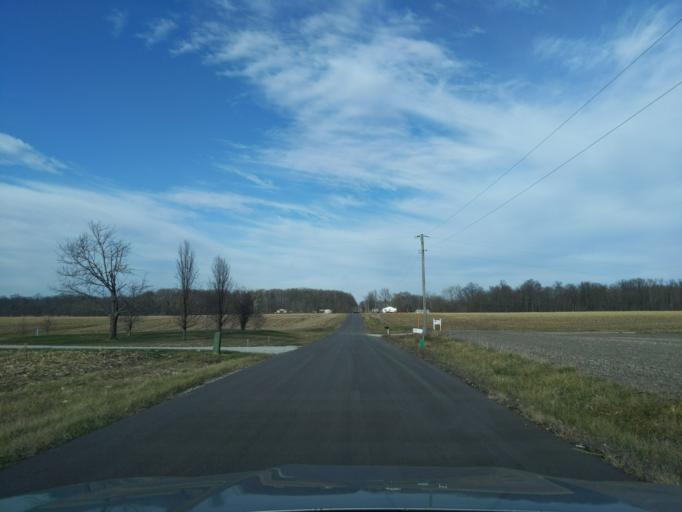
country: US
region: Indiana
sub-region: Decatur County
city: Greensburg
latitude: 39.2222
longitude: -85.4296
